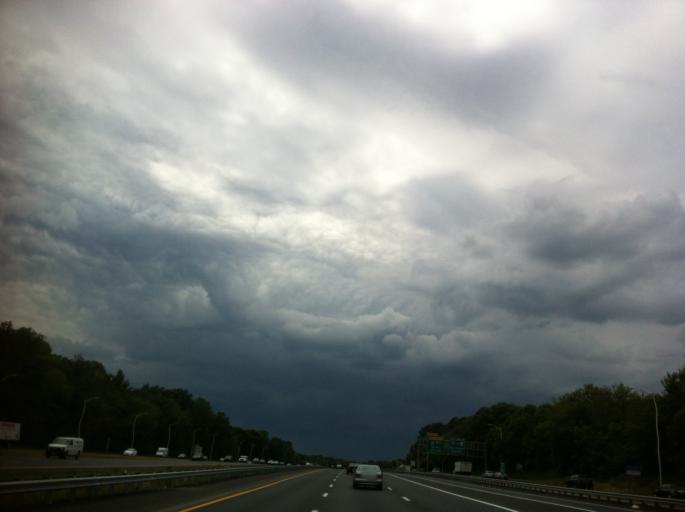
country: US
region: New Jersey
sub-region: Morris County
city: East Hanover
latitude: 40.8628
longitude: -74.3583
